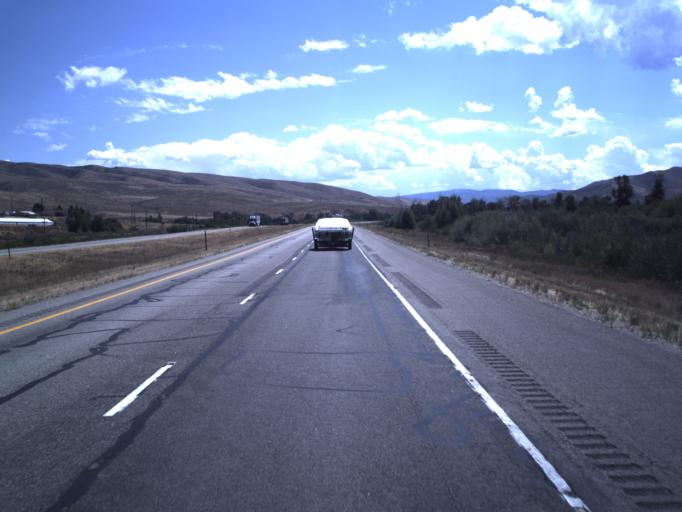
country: US
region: Utah
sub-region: Summit County
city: Coalville
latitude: 41.0350
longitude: -111.5091
